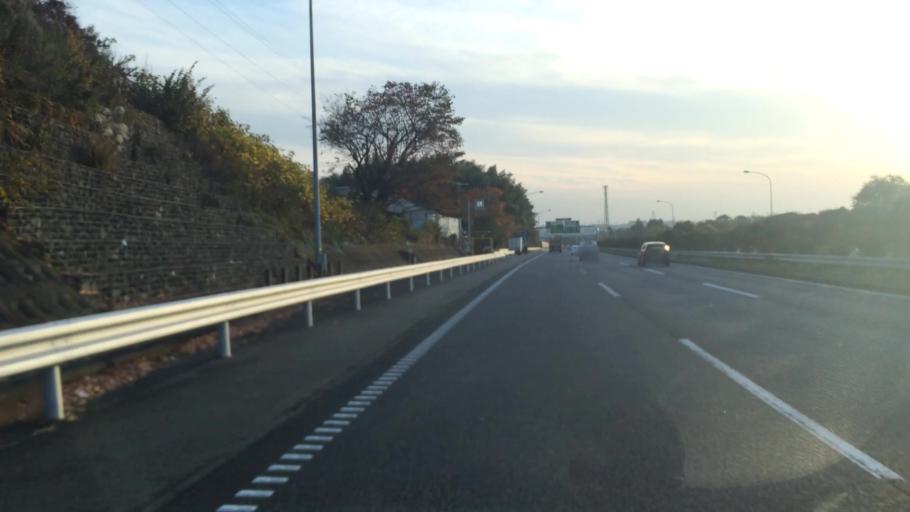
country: JP
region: Kanagawa
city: Yokohama
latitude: 35.5319
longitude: 139.5993
